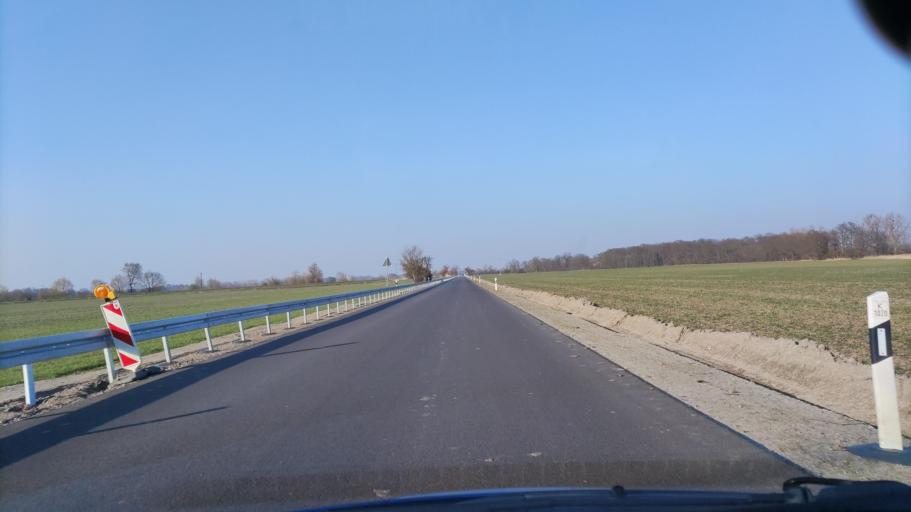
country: DE
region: Saxony-Anhalt
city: Seehausen
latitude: 52.9117
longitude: 11.7528
